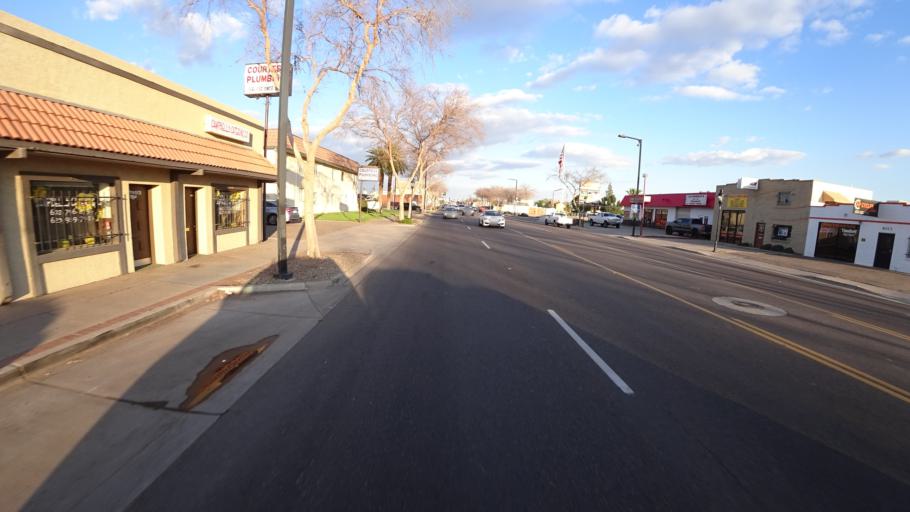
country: US
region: Arizona
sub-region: Maricopa County
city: Glendale
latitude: 33.5386
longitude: -112.1898
